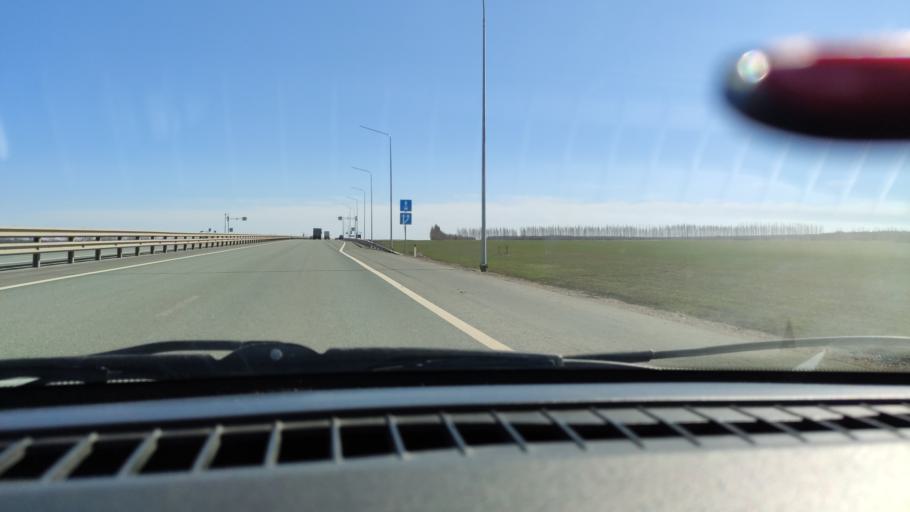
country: RU
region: Bashkortostan
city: Tolbazy
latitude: 54.1765
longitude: 55.8999
